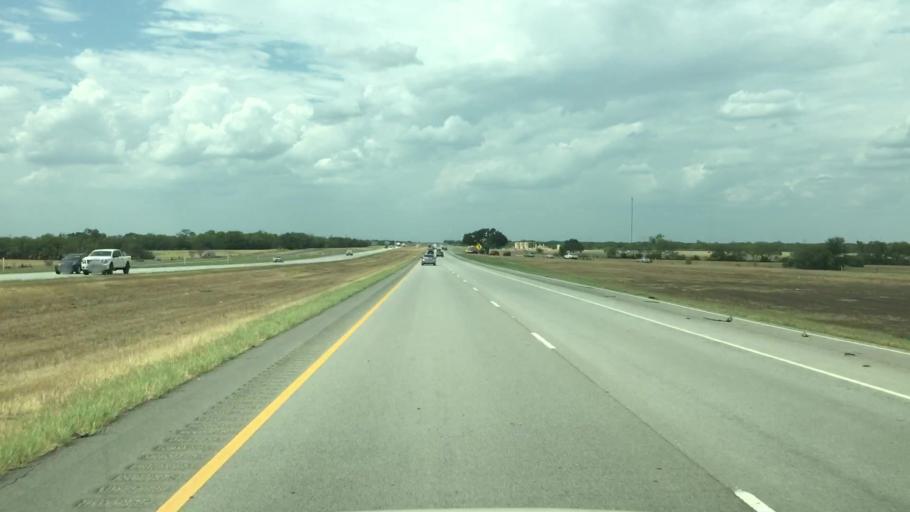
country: US
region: Texas
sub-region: Live Oak County
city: Three Rivers
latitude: 28.5302
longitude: -98.1876
